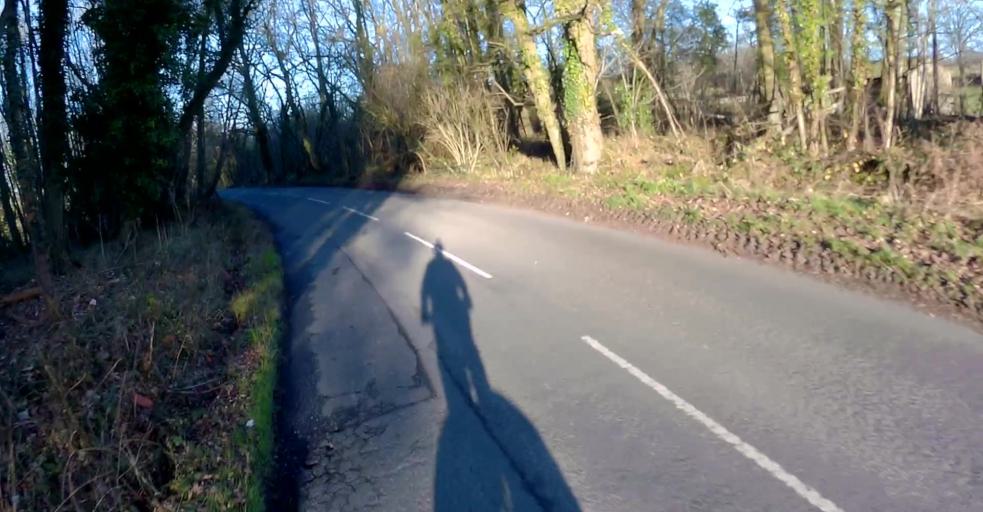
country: GB
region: England
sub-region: Hampshire
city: Hook
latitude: 51.2838
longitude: -0.9824
